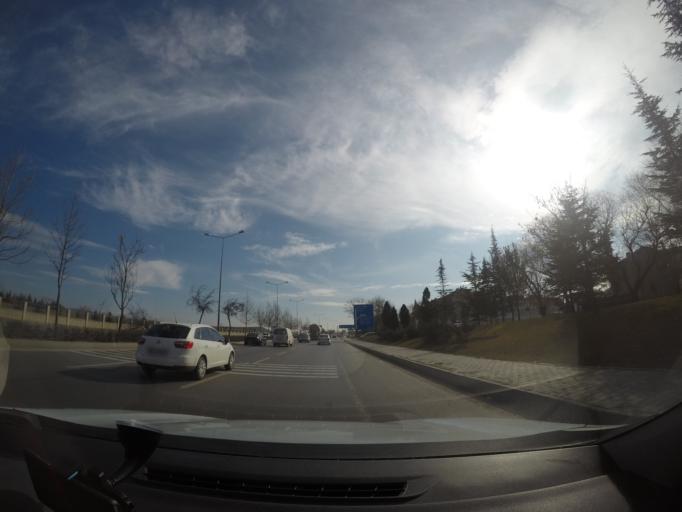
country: TR
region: Eskisehir
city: Eskisehir
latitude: 39.7971
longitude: 30.5250
